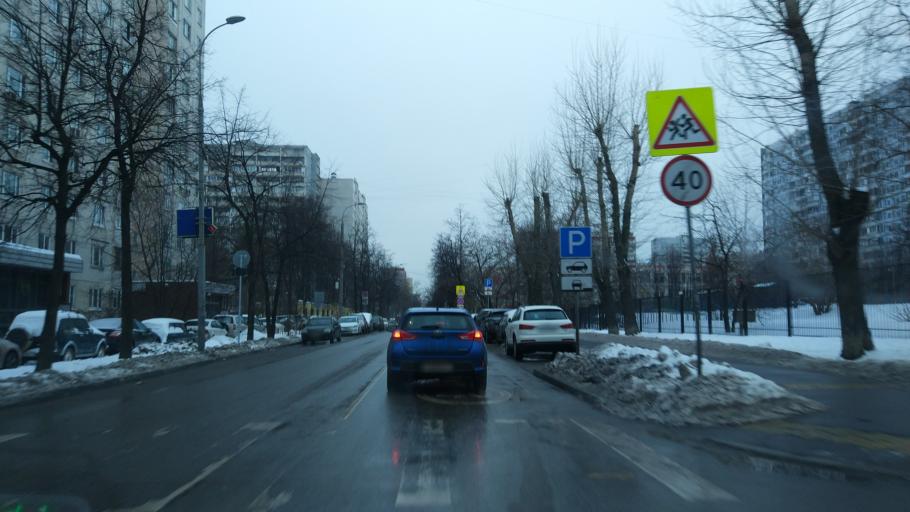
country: RU
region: Moskovskaya
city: Izmaylovo
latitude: 55.7913
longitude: 37.8149
